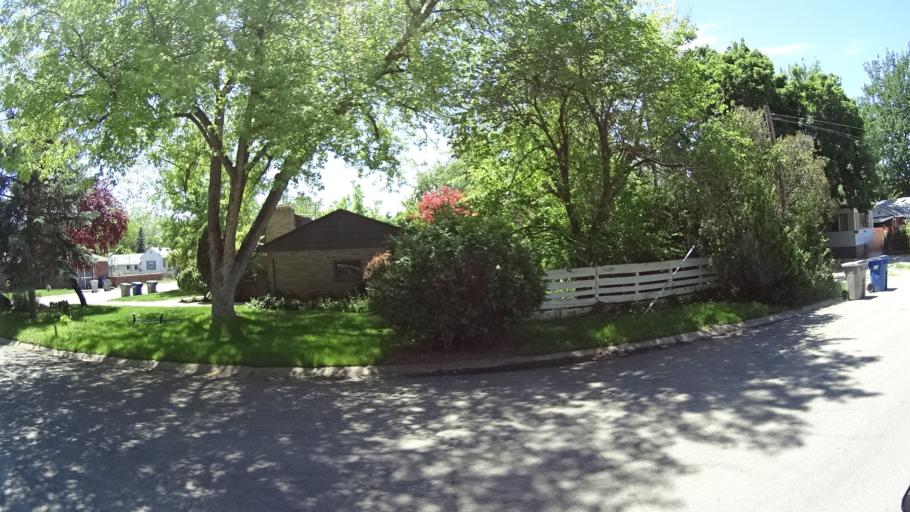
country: US
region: Idaho
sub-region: Ada County
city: Garden City
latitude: 43.5989
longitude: -116.2325
